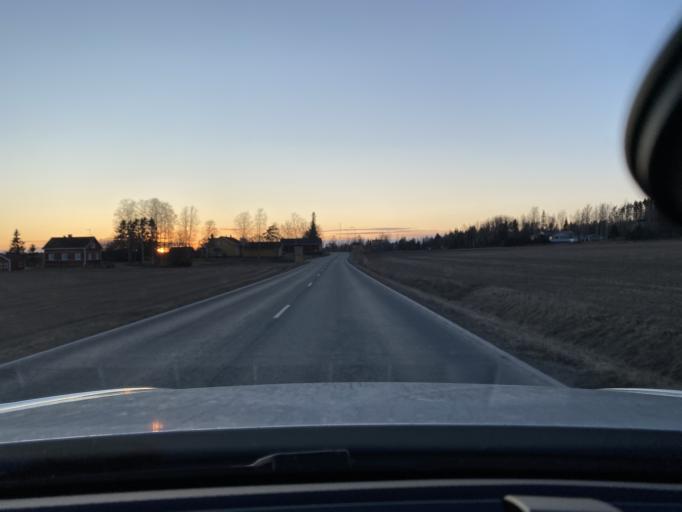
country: FI
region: Pirkanmaa
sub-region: Lounais-Pirkanmaa
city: Punkalaidun
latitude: 61.1063
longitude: 23.1383
